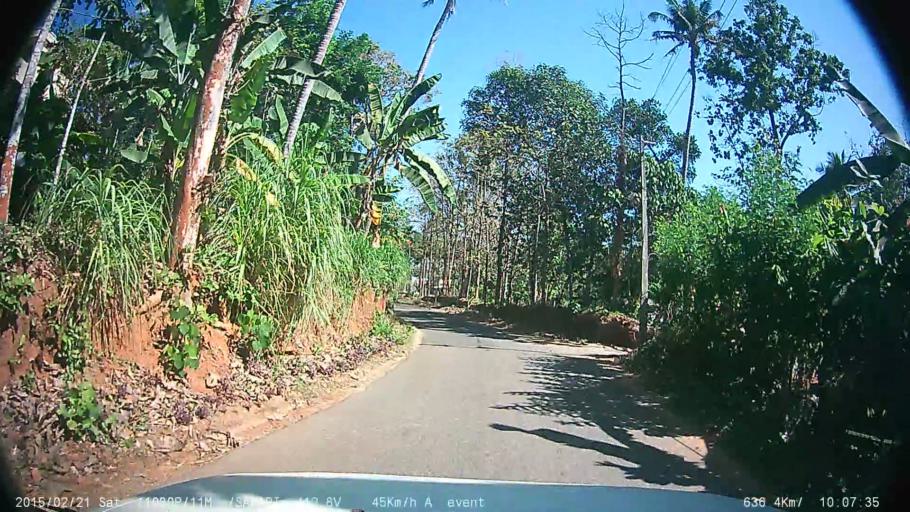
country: IN
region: Kerala
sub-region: Ernakulam
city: Piravam
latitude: 9.8733
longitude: 76.6066
